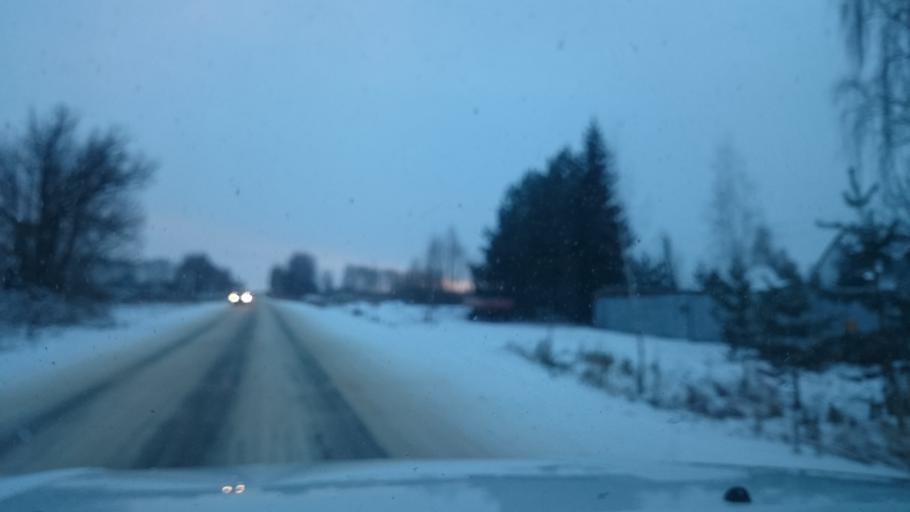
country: RU
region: Tula
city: Leninskiy
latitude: 54.2447
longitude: 37.2675
